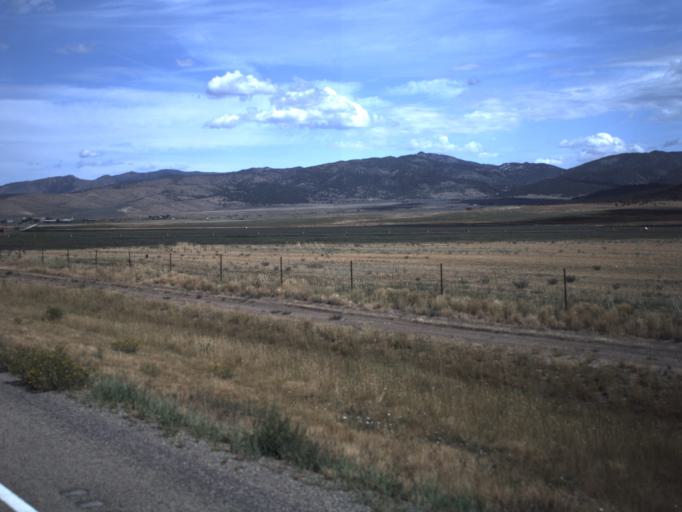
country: US
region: Utah
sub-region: Sanpete County
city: Fairview
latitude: 39.7732
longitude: -111.4885
